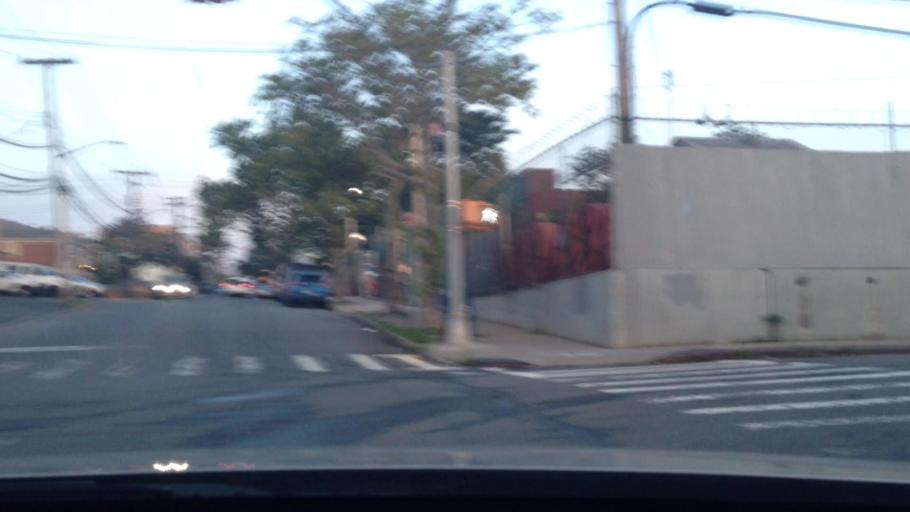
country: US
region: New York
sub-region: Bronx
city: The Bronx
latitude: 40.7786
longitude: -73.8388
